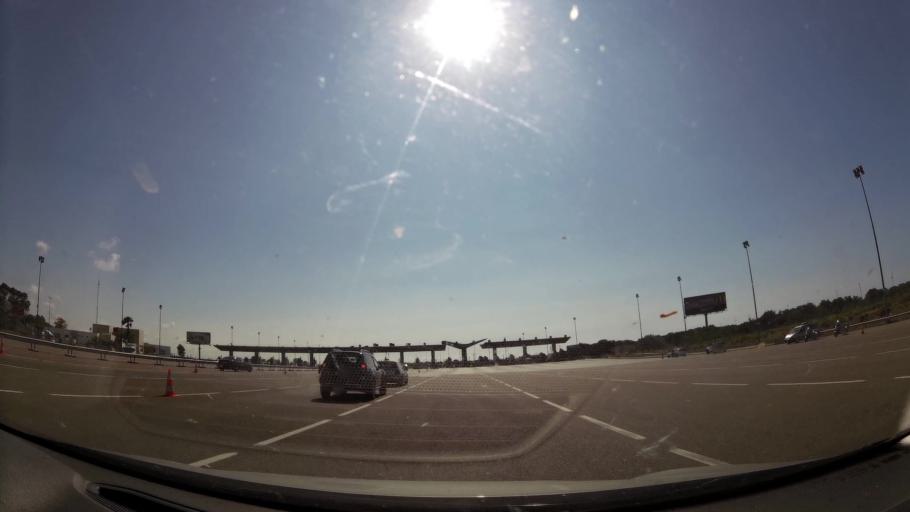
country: MA
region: Chaouia-Ouardigha
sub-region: Benslimane
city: Bouznika
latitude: 33.7983
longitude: -7.1715
